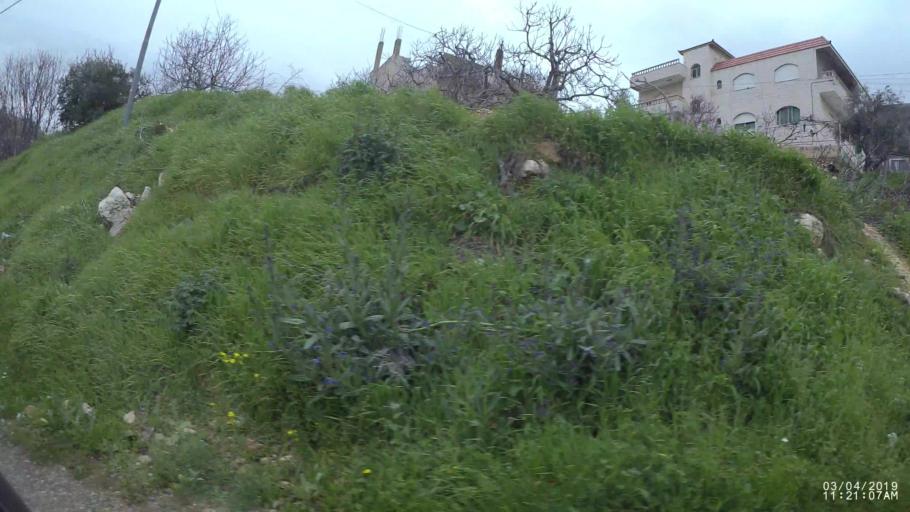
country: JO
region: Amman
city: Wadi as Sir
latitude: 31.9580
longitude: 35.8124
